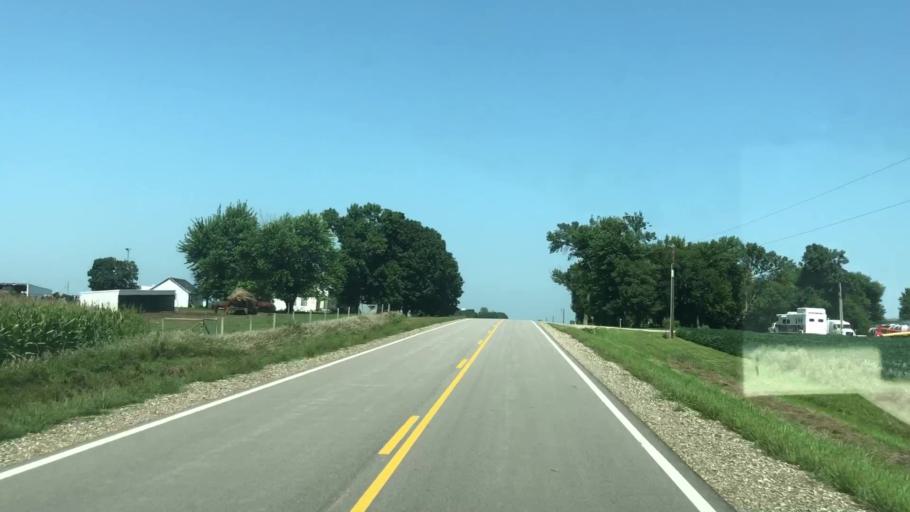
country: US
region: Iowa
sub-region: O'Brien County
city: Sanborn
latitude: 43.2603
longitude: -95.7235
